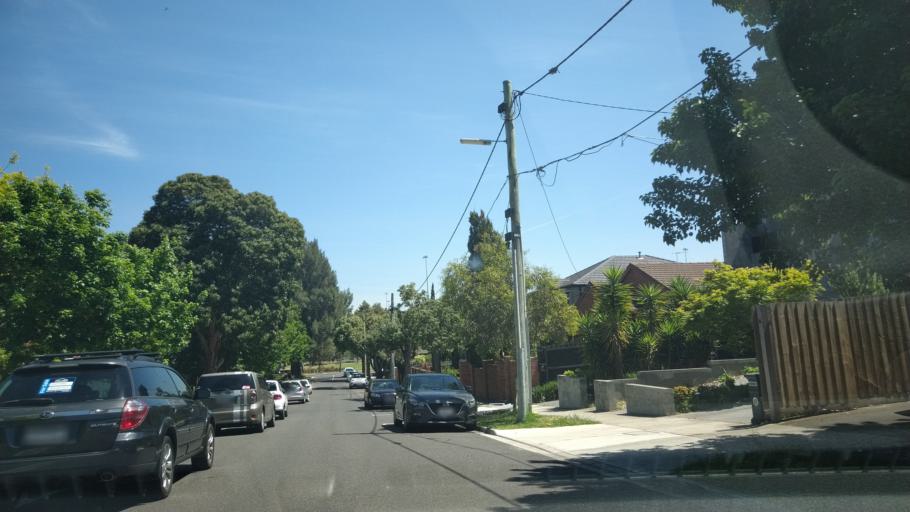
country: AU
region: Victoria
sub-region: Glen Eira
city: Caulfield South
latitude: -37.8958
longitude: 145.0289
